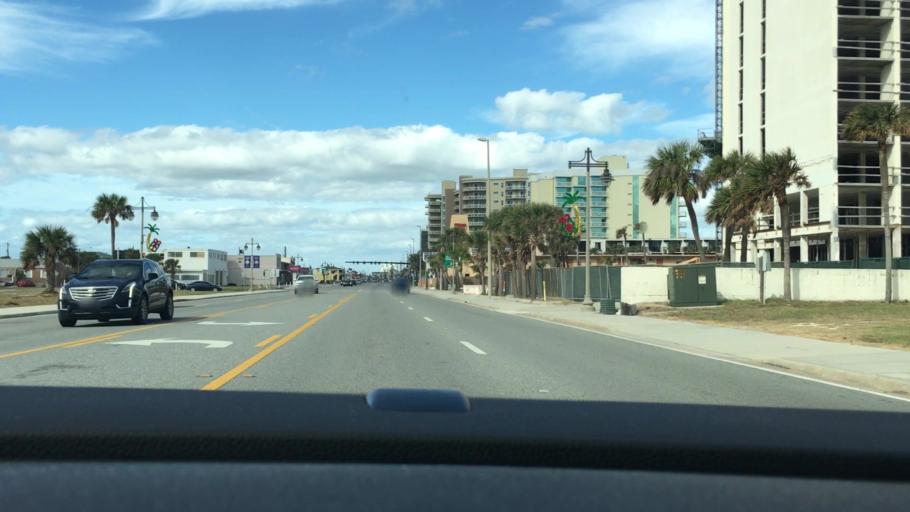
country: US
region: Florida
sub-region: Volusia County
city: Daytona Beach Shores
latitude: 29.2007
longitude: -80.9953
